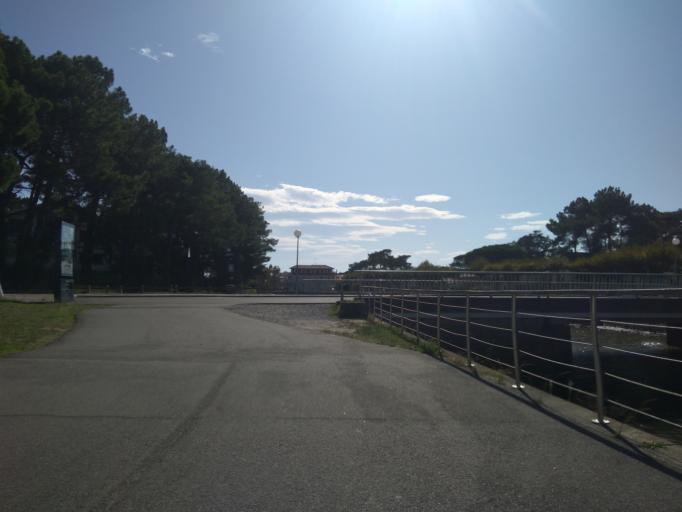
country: FR
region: Aquitaine
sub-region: Departement des Landes
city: Capbreton
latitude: 43.6491
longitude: -1.4353
